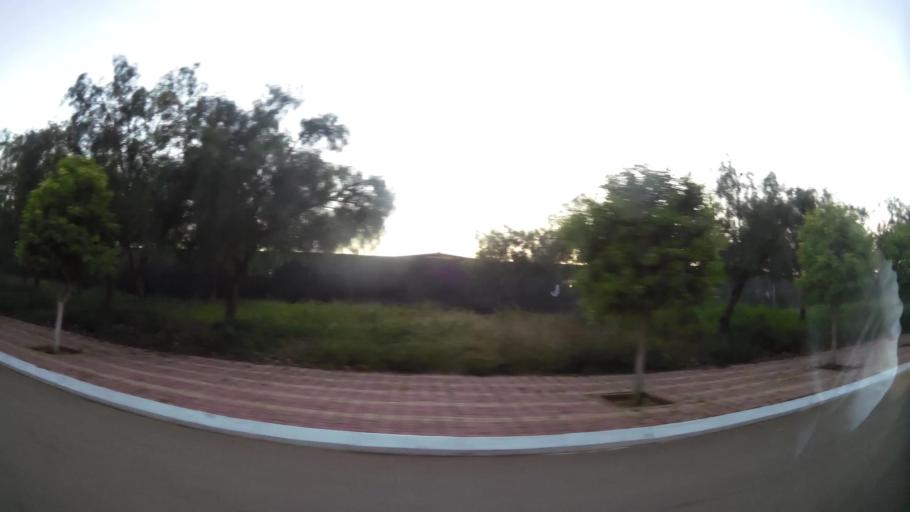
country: MA
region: Marrakech-Tensift-Al Haouz
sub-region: Kelaa-Des-Sraghna
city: Sidi Bou Othmane
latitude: 32.2128
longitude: -7.9341
